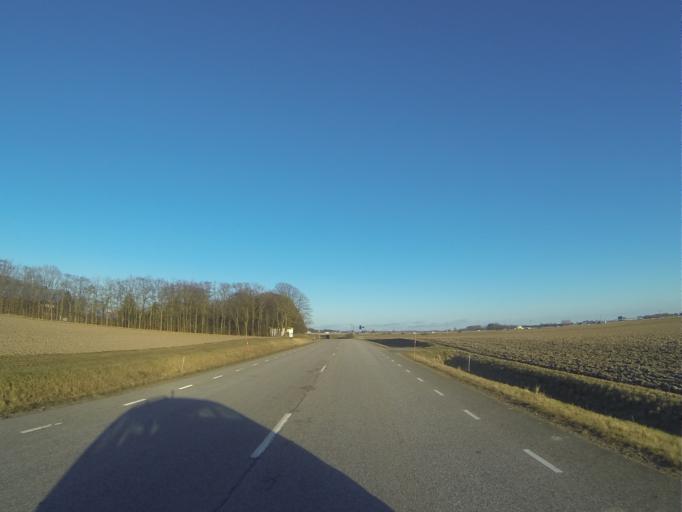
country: SE
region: Skane
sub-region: Malmo
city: Tygelsjo
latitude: 55.5432
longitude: 12.9986
